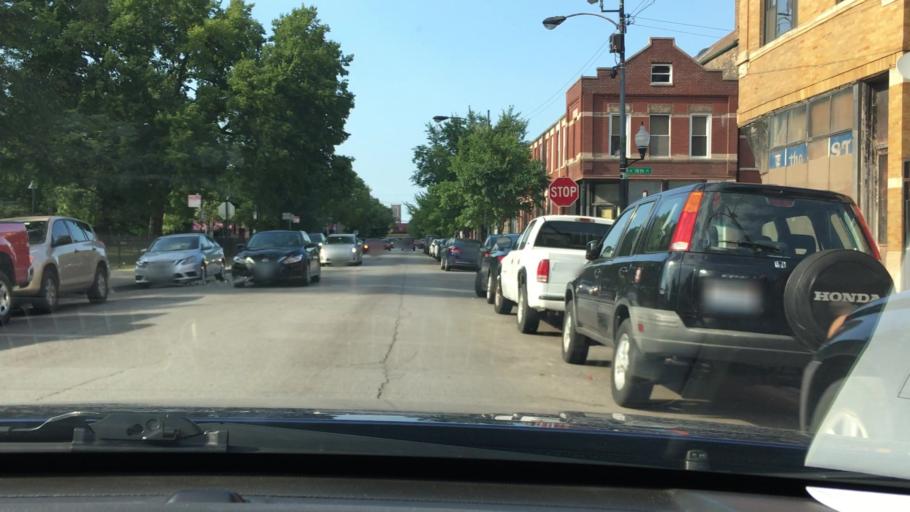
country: US
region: Illinois
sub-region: Cook County
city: Chicago
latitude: 41.8566
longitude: -87.6710
